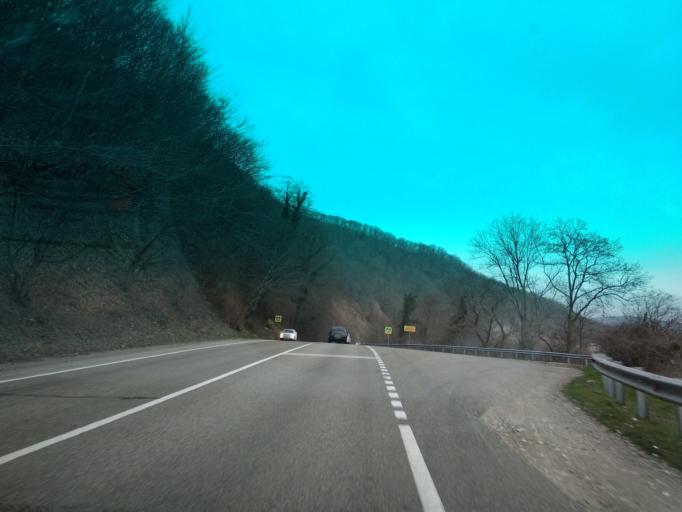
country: RU
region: Krasnodarskiy
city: Ol'ginka
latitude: 44.2223
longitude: 38.8951
